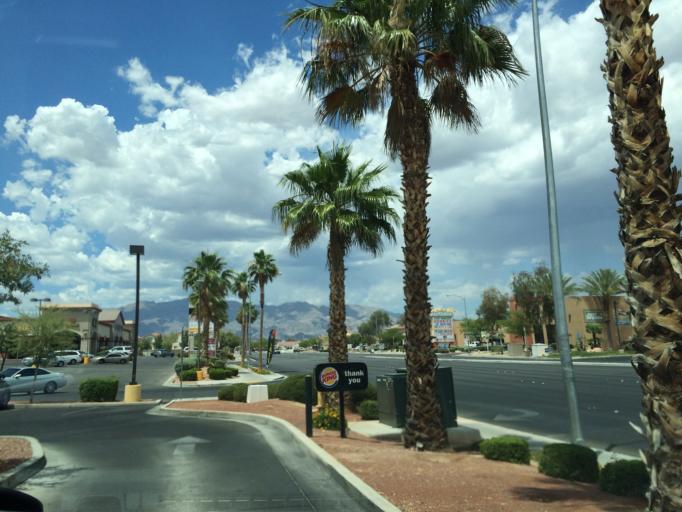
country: US
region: Nevada
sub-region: Clark County
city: North Las Vegas
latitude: 36.2618
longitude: -115.1803
